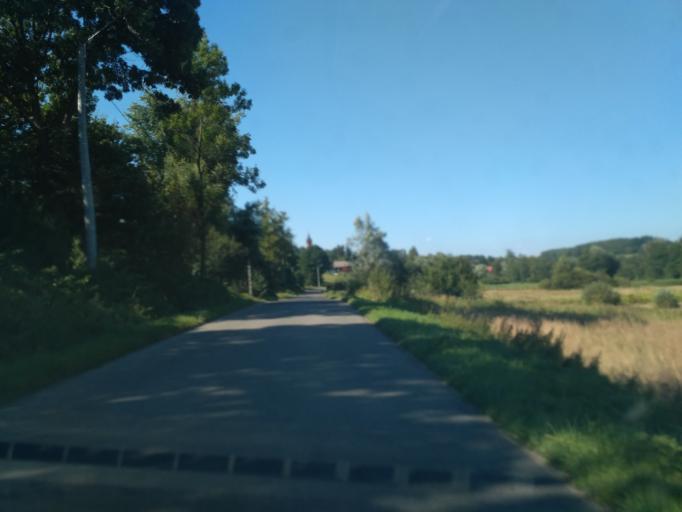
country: PL
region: Subcarpathian Voivodeship
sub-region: Powiat strzyzowski
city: Wysoka Strzyzowska
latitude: 49.8275
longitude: 21.7390
